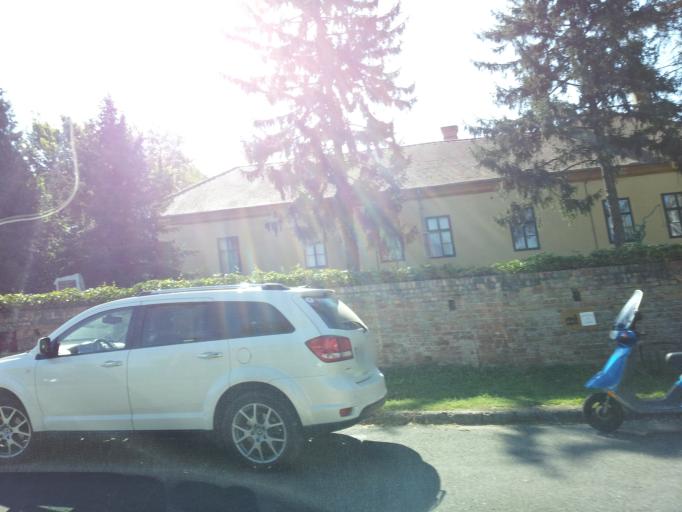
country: HU
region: Somogy
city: Balatonfoldvar
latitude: 46.8679
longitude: 17.9140
